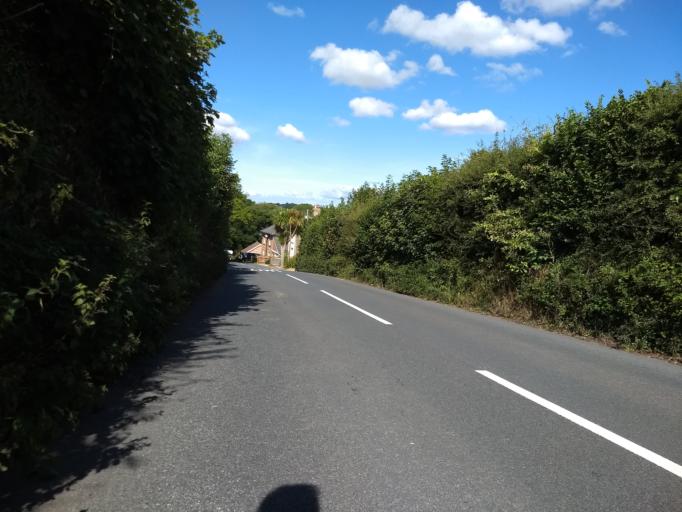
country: GB
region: England
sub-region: Isle of Wight
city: Ryde
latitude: 50.7107
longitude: -1.1802
